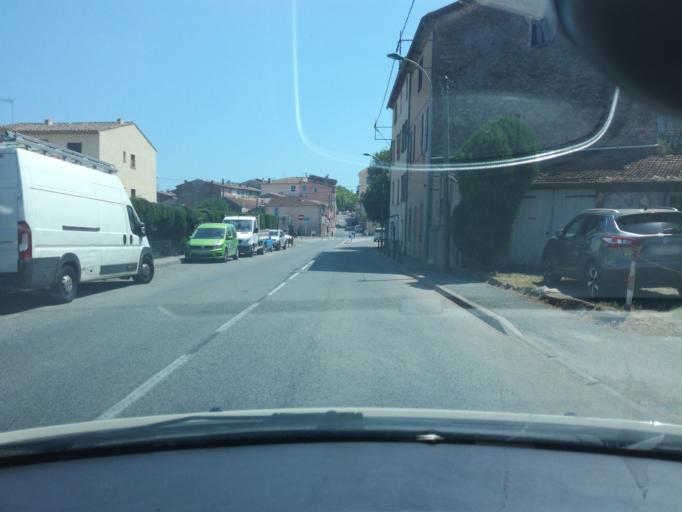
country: FR
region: Provence-Alpes-Cote d'Azur
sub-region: Departement du Var
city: Le Muy
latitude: 43.4756
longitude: 6.5667
